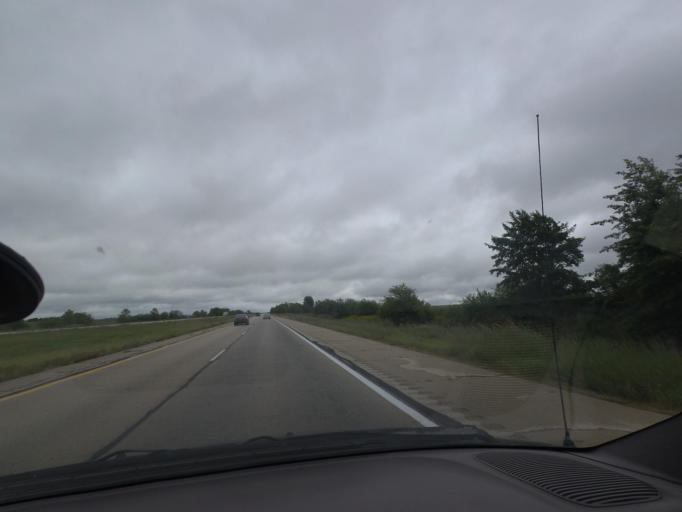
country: US
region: Illinois
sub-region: Piatt County
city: Cerro Gordo
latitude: 40.0189
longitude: -88.7173
